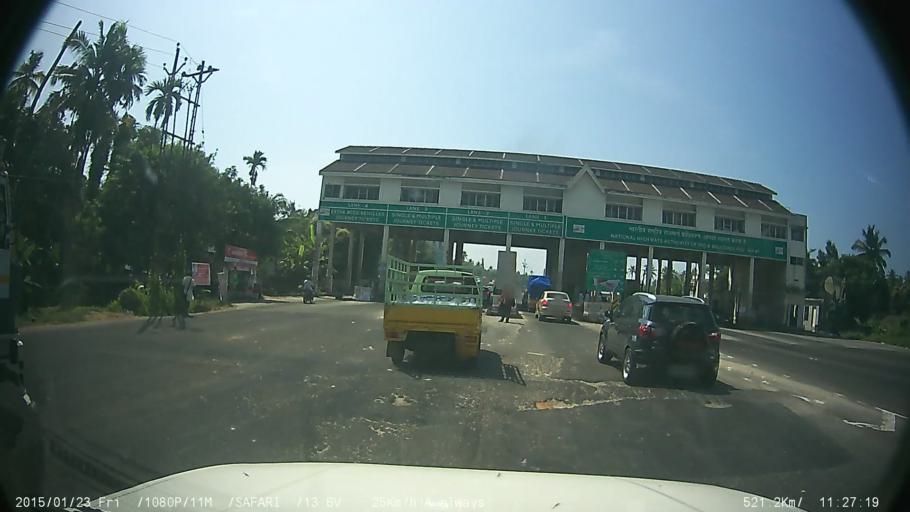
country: IN
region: Kerala
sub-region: Alappuzha
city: Arukutti
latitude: 9.8957
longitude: 76.3137
